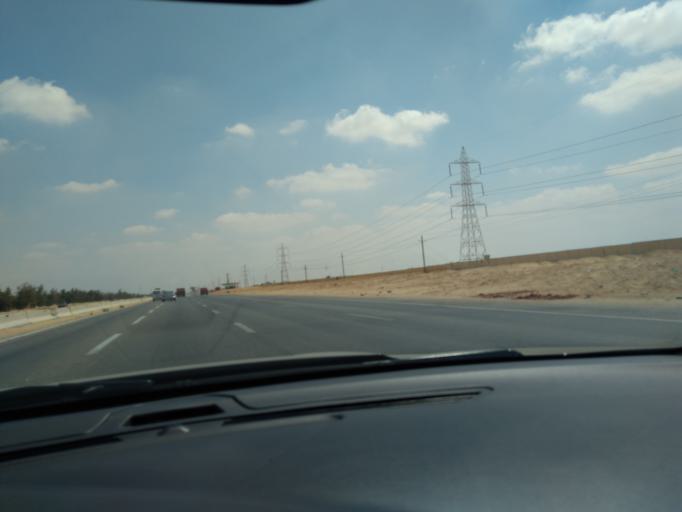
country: EG
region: Al Isma'iliyah
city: At Tall al Kabir
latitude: 30.3961
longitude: 31.9768
